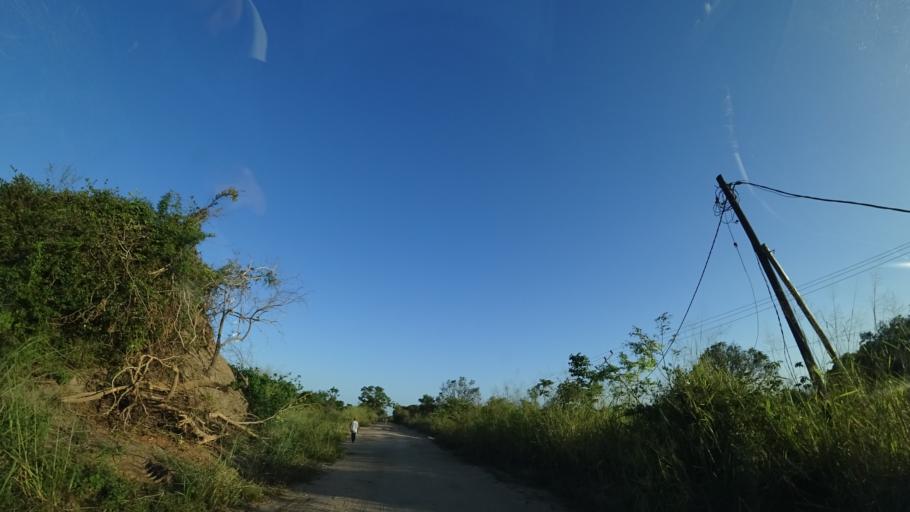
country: MZ
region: Sofala
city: Dondo
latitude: -19.3974
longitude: 34.7089
